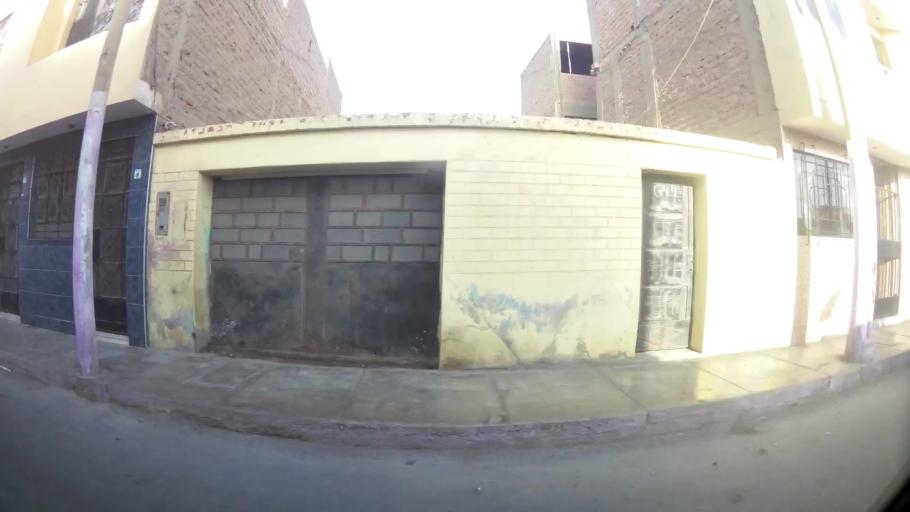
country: PE
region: Lima
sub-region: Huaura
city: Huacho
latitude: -11.1141
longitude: -77.6064
